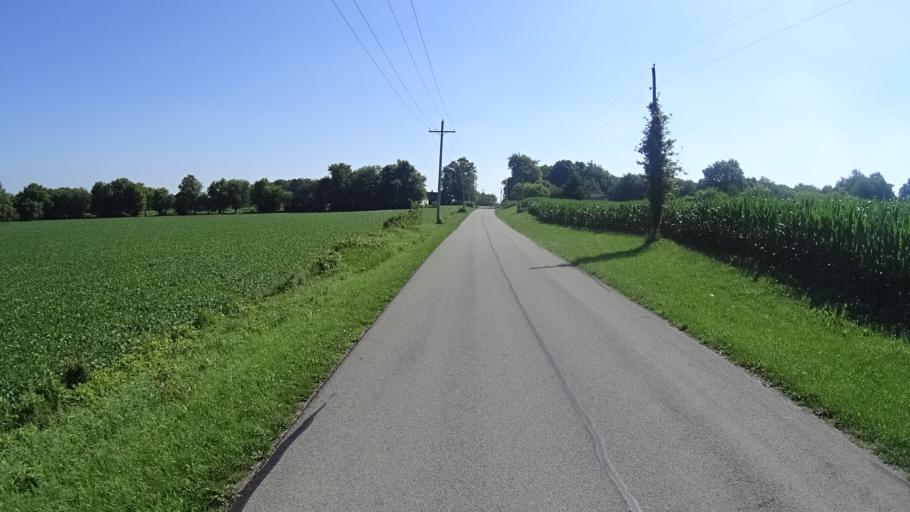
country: US
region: Indiana
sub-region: Madison County
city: Ingalls
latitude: 39.9700
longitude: -85.7838
